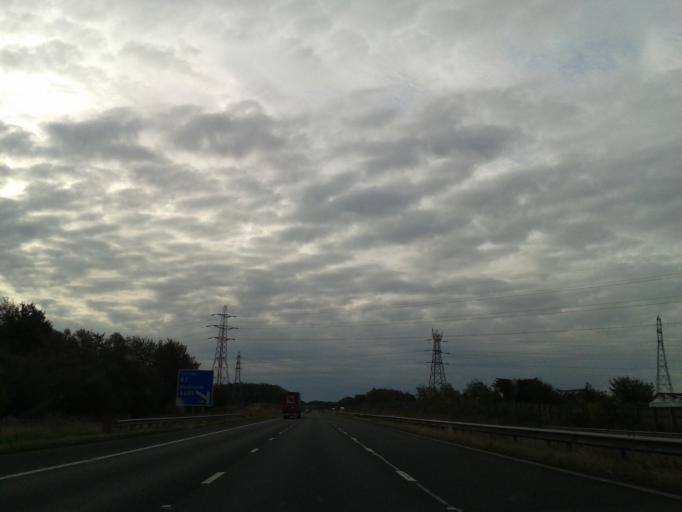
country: GB
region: England
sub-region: Cumbria
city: Carlisle
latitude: 54.9441
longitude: -2.9701
